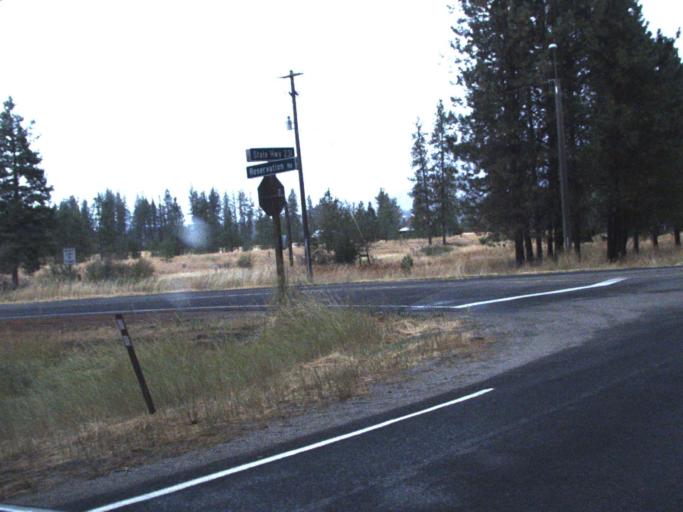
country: US
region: Washington
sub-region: Spokane County
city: Deer Park
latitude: 47.9945
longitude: -117.7264
